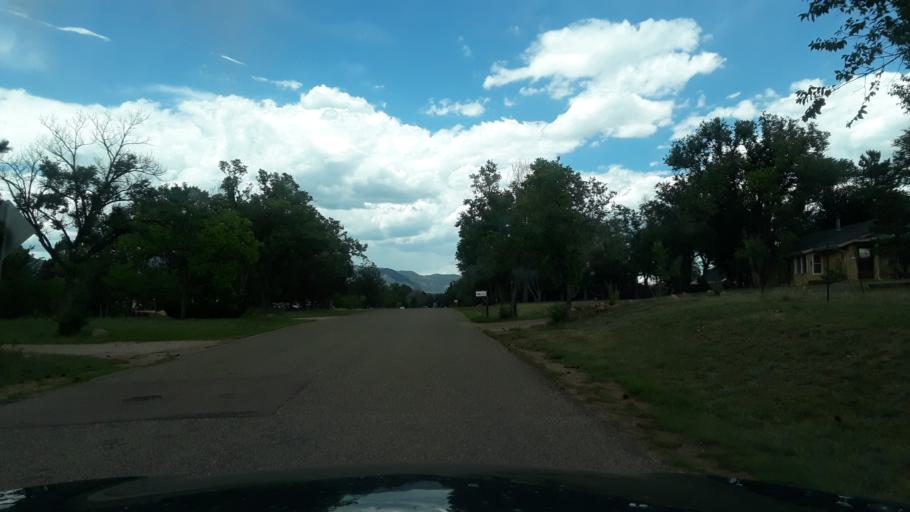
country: US
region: Colorado
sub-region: El Paso County
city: Air Force Academy
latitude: 38.9407
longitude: -104.8142
